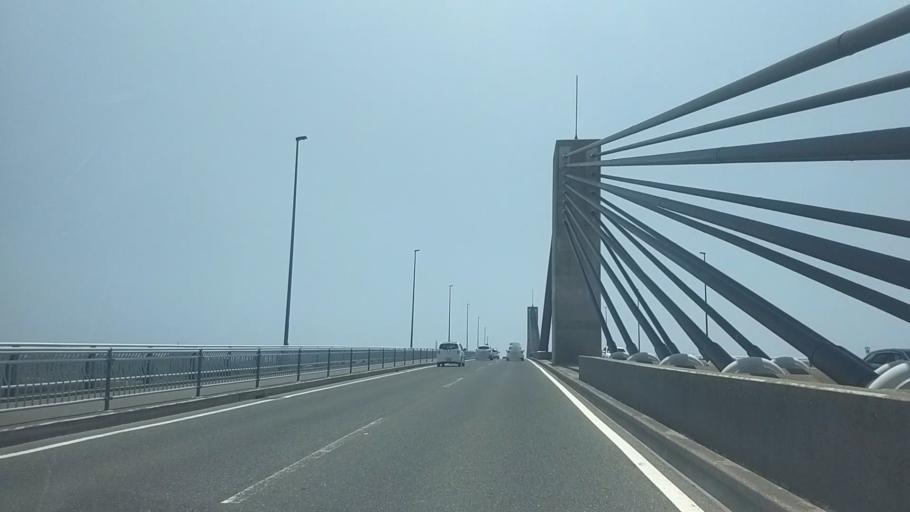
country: JP
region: Shizuoka
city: Hamamatsu
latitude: 34.6932
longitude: 137.6476
